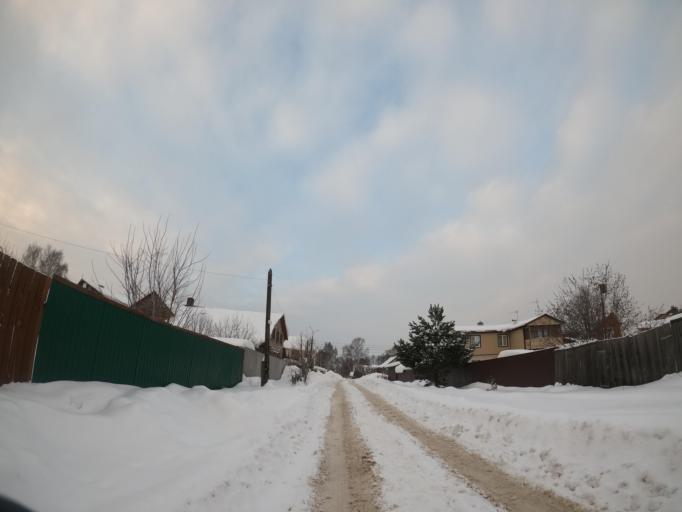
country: RU
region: Moskovskaya
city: Pavlovskiy Posad
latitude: 55.7713
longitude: 38.6312
